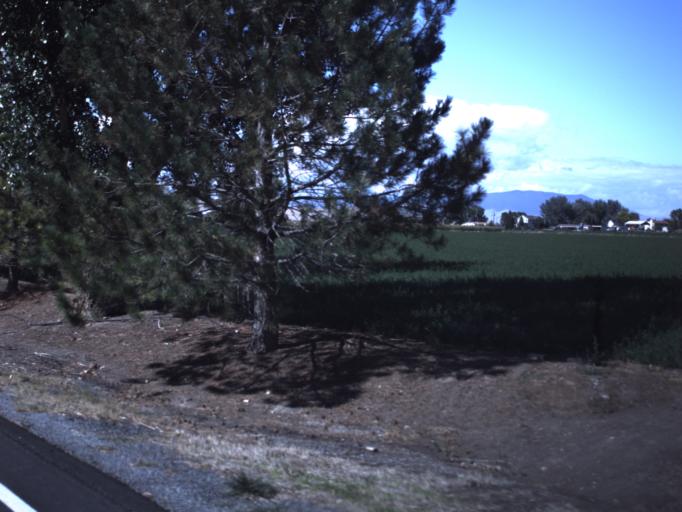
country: US
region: Utah
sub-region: Utah County
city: Benjamin
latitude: 40.0980
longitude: -111.7452
